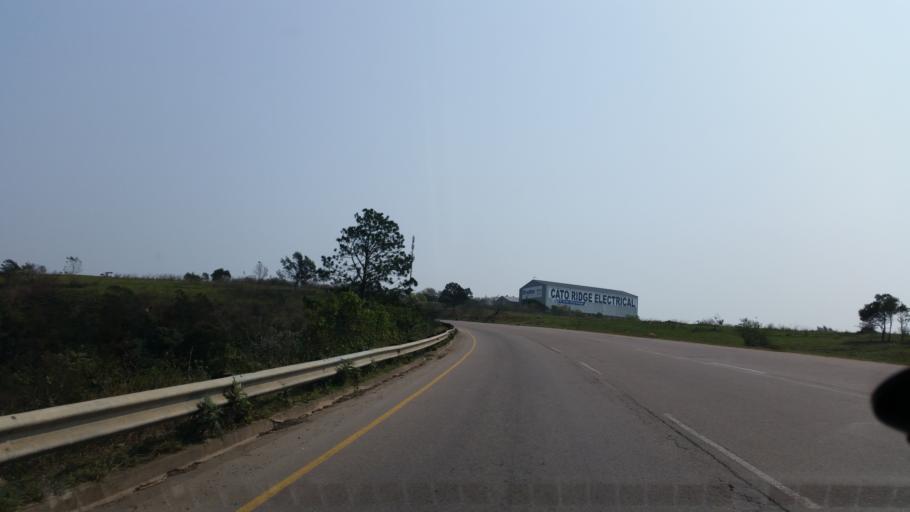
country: ZA
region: KwaZulu-Natal
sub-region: eThekwini Metropolitan Municipality
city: Mpumalanga
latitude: -29.7311
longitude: 30.6494
